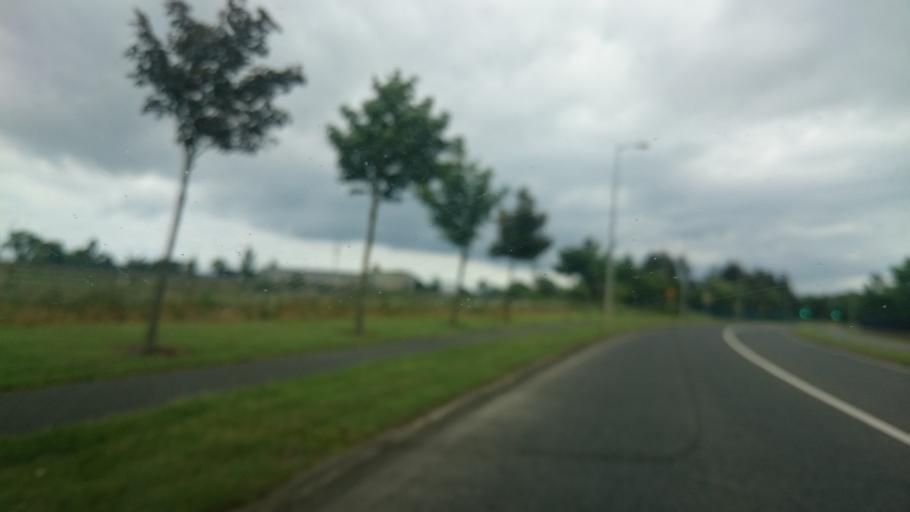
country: IE
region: Leinster
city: Lusk
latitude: 53.5295
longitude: -6.1599
